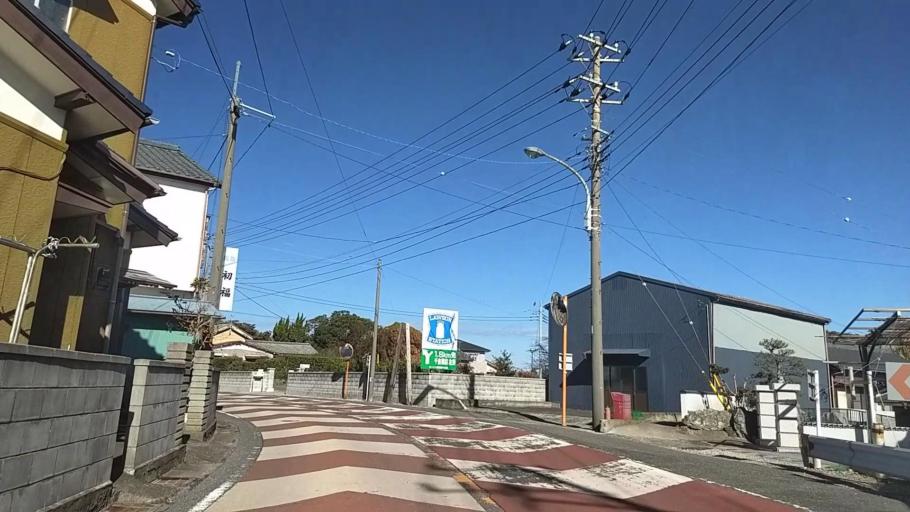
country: JP
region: Chiba
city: Tateyama
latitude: 34.9482
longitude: 139.9630
